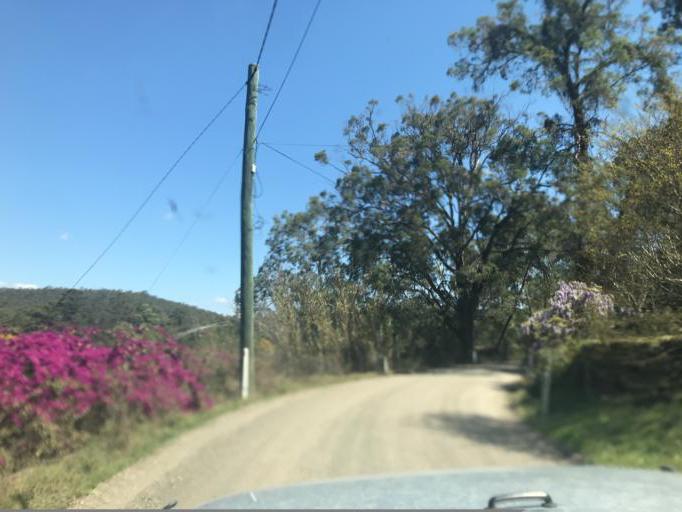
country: AU
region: New South Wales
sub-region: Hawkesbury
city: Pitt Town
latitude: -33.4176
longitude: 150.9084
